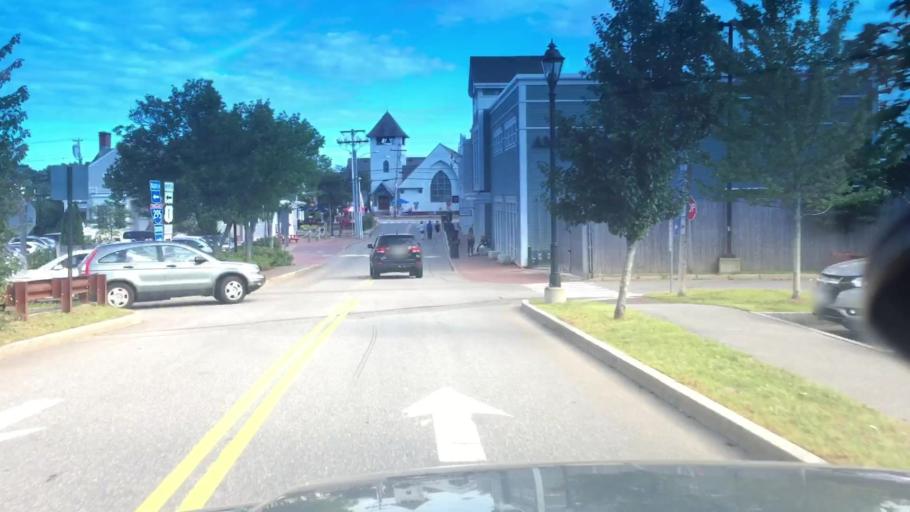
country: US
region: Maine
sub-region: Cumberland County
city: Freeport
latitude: 43.8568
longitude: -70.1063
